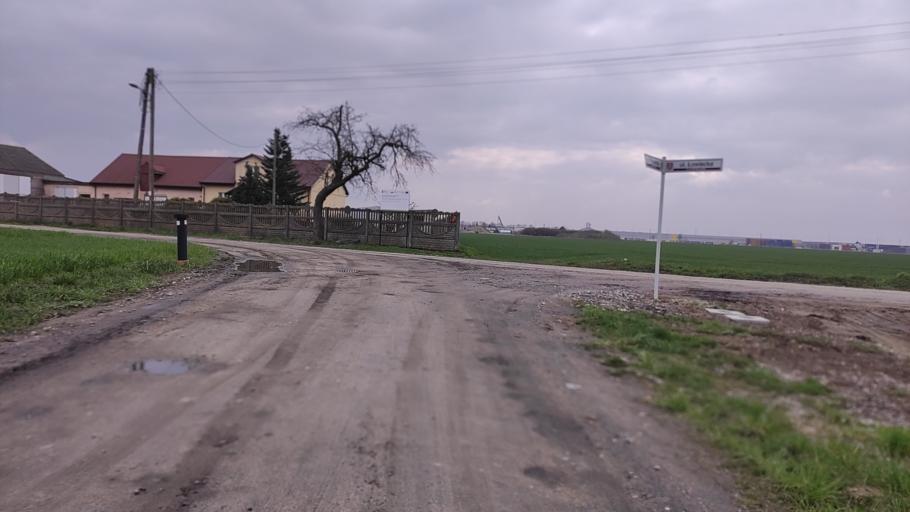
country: PL
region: Greater Poland Voivodeship
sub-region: Powiat poznanski
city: Swarzedz
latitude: 52.4066
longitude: 17.1387
